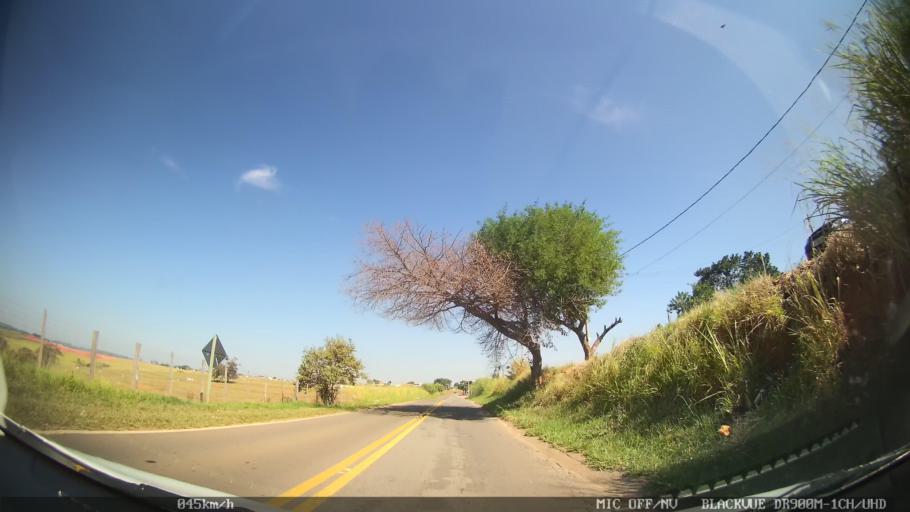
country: BR
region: Sao Paulo
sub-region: Valinhos
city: Valinhos
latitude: -23.0297
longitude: -47.0984
